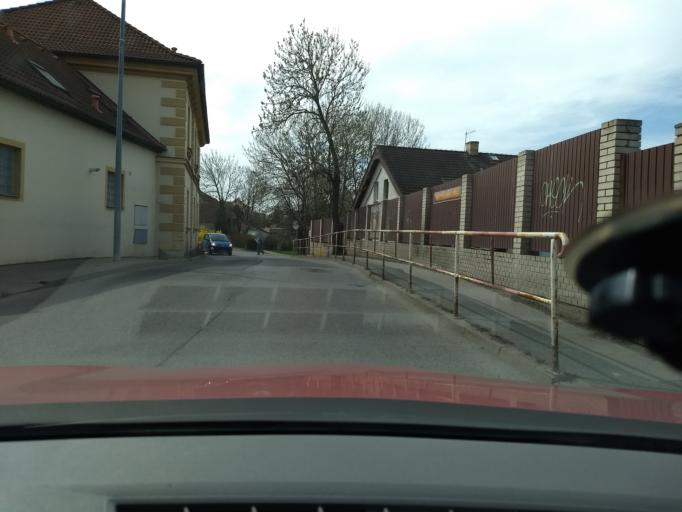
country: CZ
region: Central Bohemia
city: Hostivice
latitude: 50.0629
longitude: 14.2852
